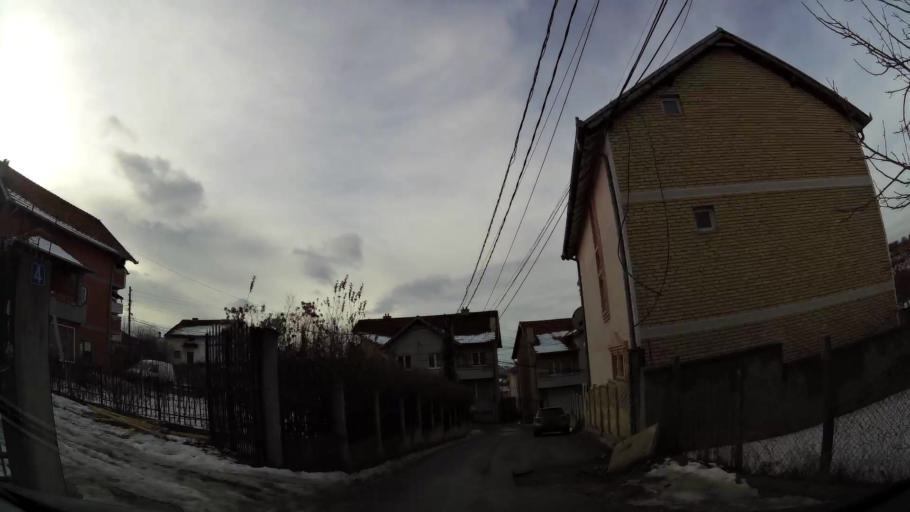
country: XK
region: Pristina
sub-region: Komuna e Prishtines
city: Pristina
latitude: 42.6712
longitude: 21.1870
